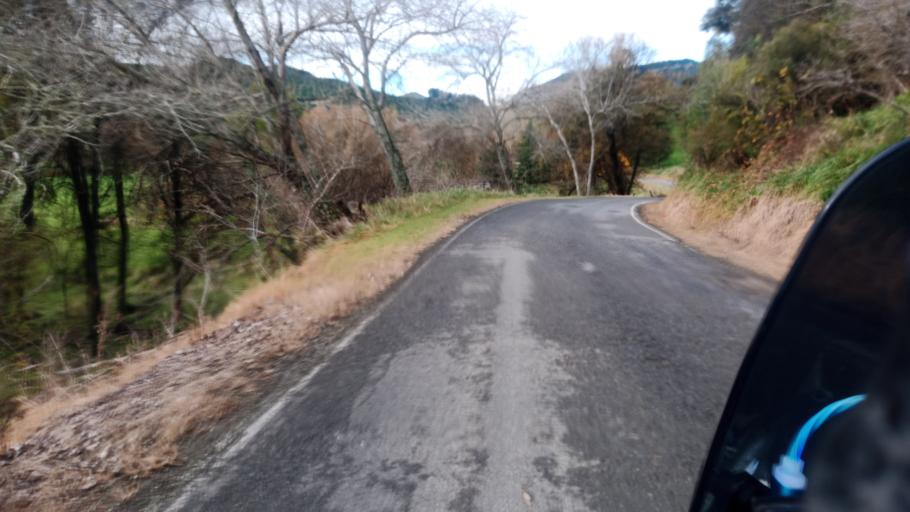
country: NZ
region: Gisborne
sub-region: Gisborne District
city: Gisborne
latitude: -38.4097
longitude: 177.9440
